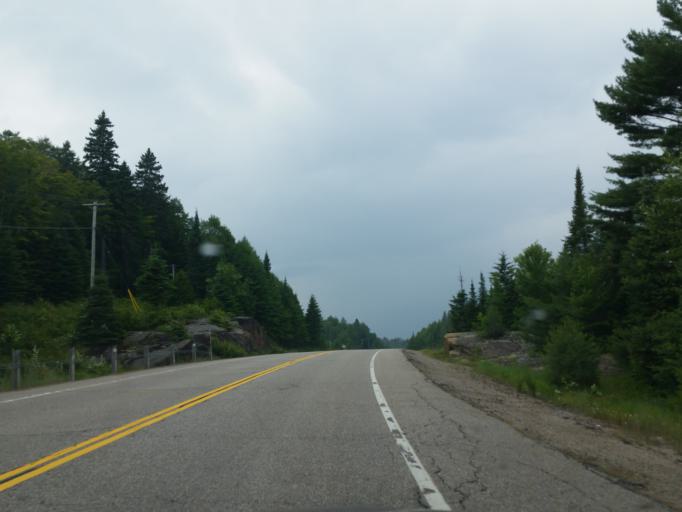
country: CA
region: Ontario
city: Huntsville
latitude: 45.5638
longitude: -78.5470
